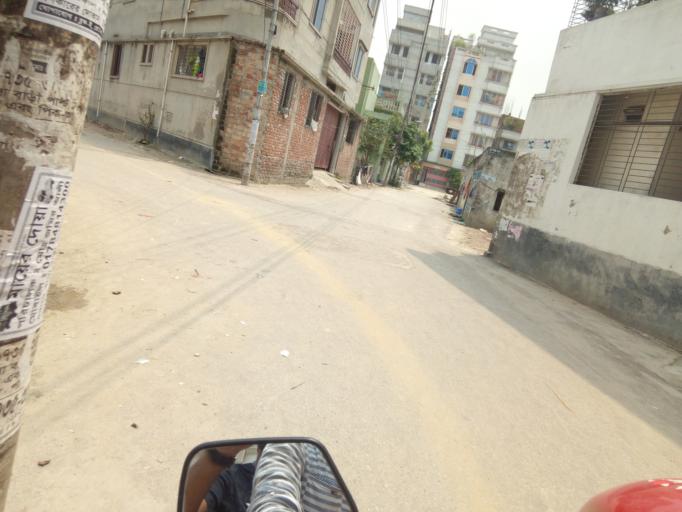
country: BD
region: Dhaka
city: Paltan
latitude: 23.7515
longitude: 90.4381
